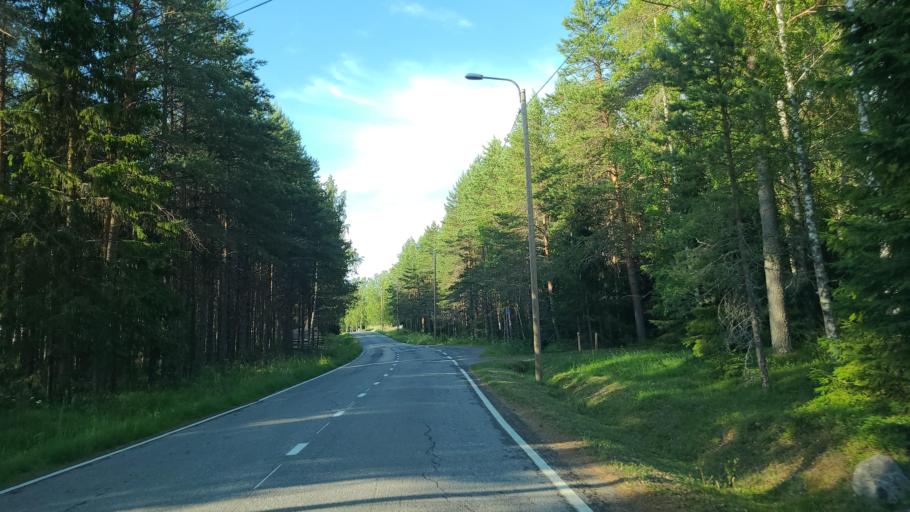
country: FI
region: Ostrobothnia
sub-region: Vaasa
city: Replot
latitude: 63.3516
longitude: 21.3008
